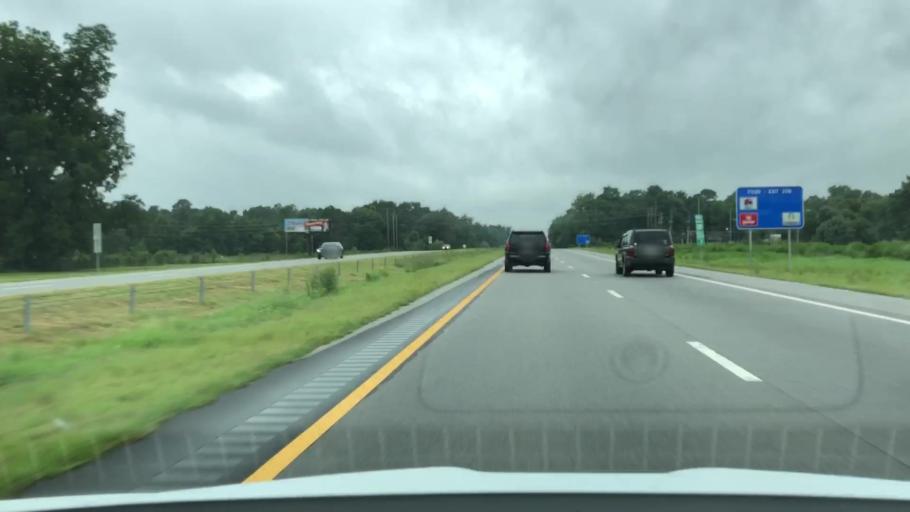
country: US
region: North Carolina
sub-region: Wayne County
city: Elroy
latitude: 35.4182
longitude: -77.9216
